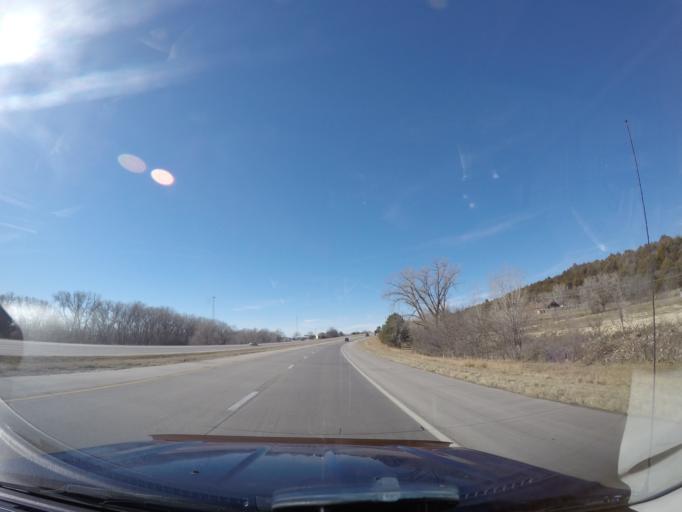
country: US
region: Kansas
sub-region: Geary County
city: Junction City
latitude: 38.9998
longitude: -96.8522
